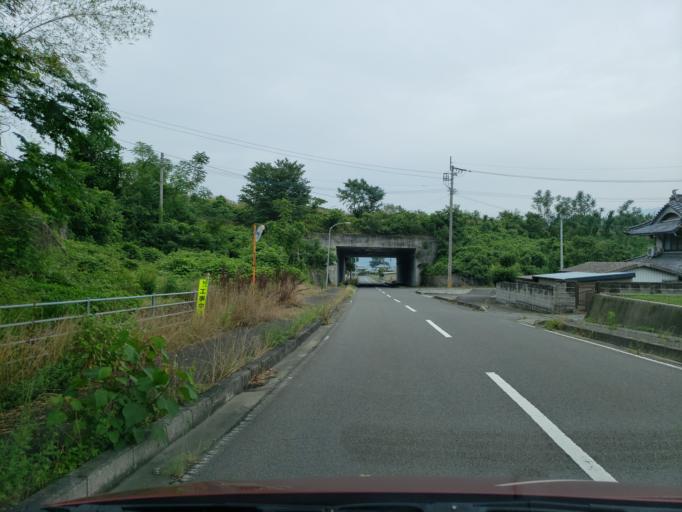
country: JP
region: Tokushima
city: Wakimachi
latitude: 34.0999
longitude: 134.2263
